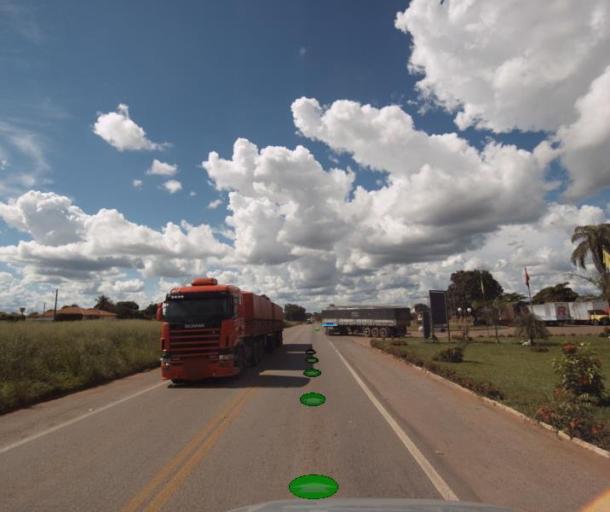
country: BR
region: Goias
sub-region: Porangatu
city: Porangatu
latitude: -13.4455
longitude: -49.1338
